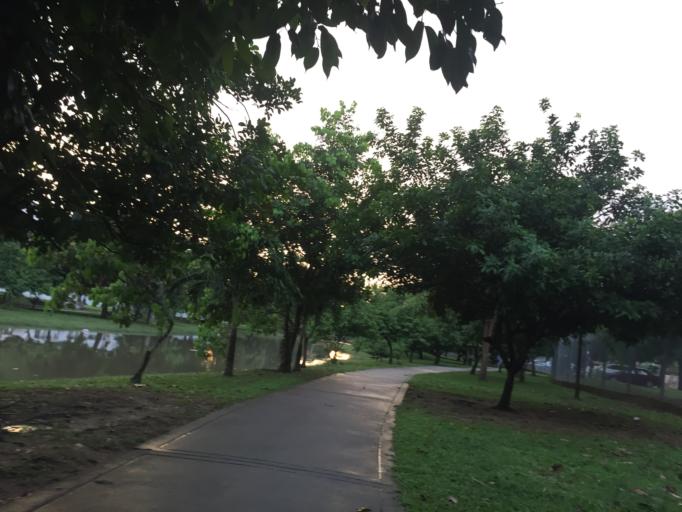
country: MY
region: Selangor
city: Klang
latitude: 2.9883
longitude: 101.4354
